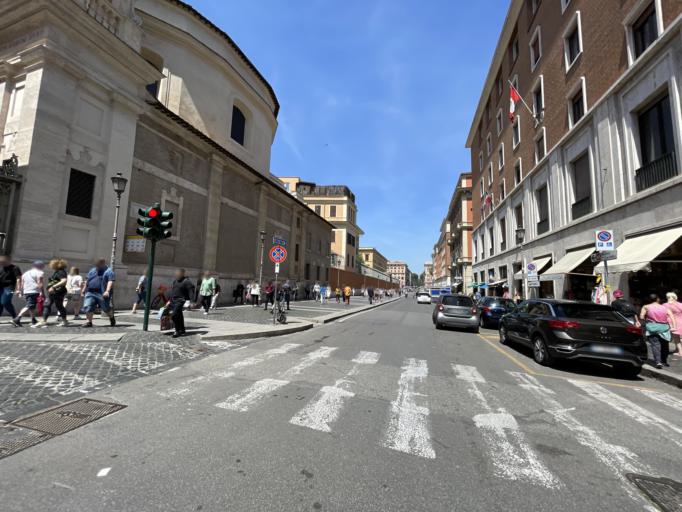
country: VA
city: Vatican City
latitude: 41.9039
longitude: 12.4577
